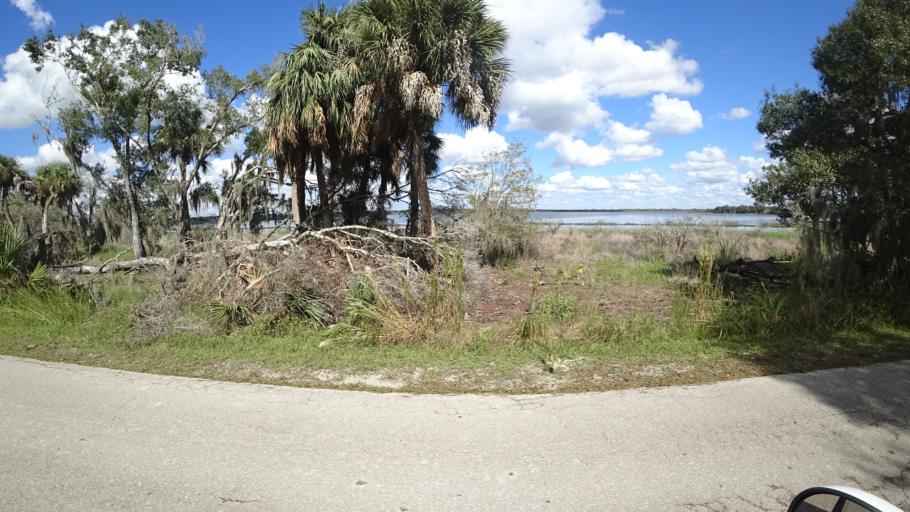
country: US
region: Florida
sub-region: Sarasota County
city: Lake Sarasota
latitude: 27.2710
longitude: -82.2771
